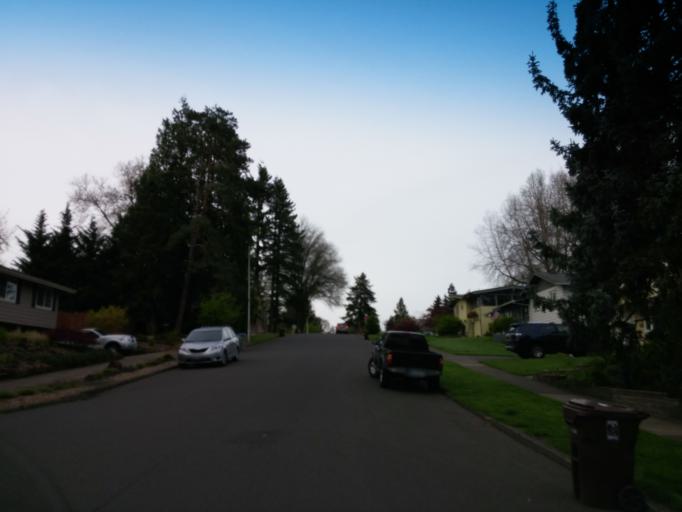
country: US
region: Oregon
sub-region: Washington County
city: Cedar Hills
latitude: 45.5119
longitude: -122.8049
